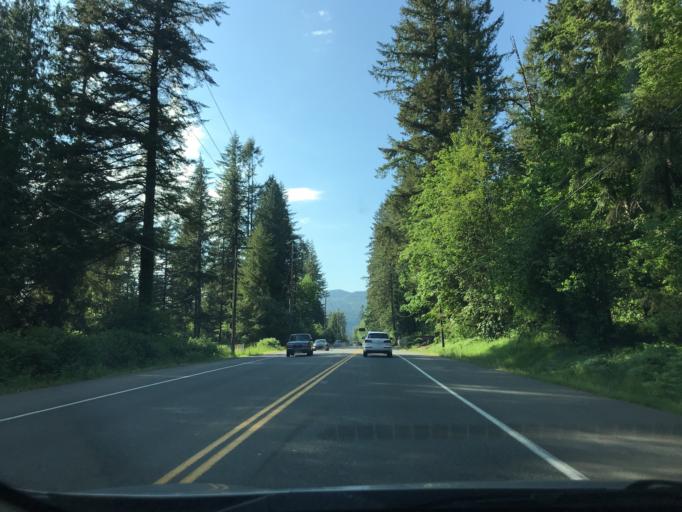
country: US
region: Washington
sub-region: King County
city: Mirrormont
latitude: 47.4655
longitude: -122.0161
